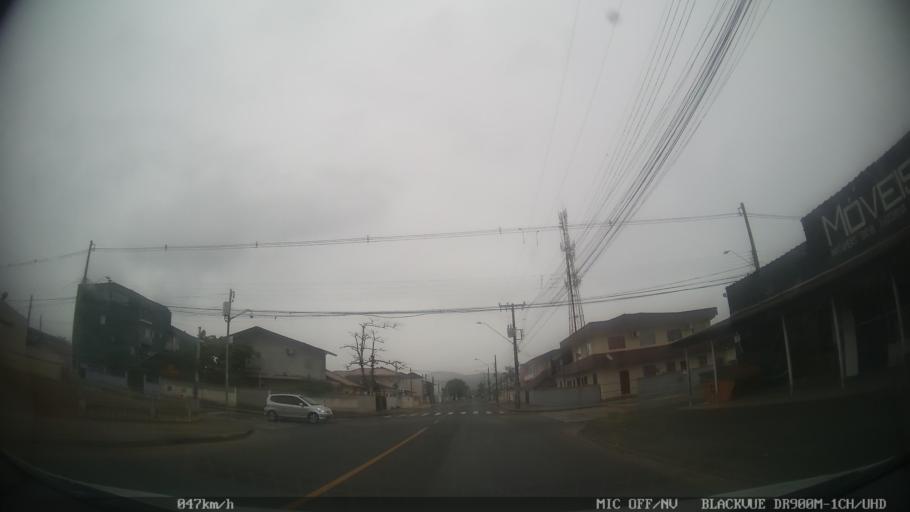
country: BR
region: Santa Catarina
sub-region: Joinville
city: Joinville
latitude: -26.2691
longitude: -48.8018
